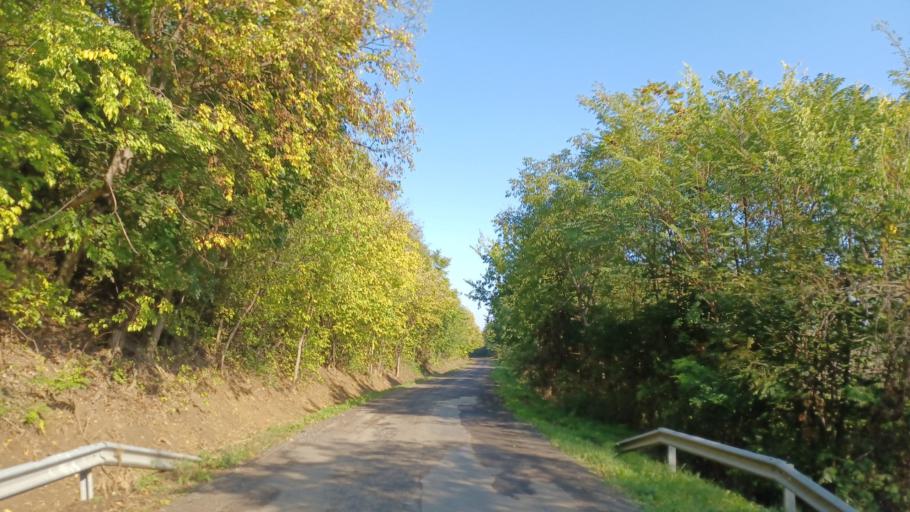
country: HU
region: Tolna
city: Szedres
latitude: 46.5314
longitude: 18.5923
